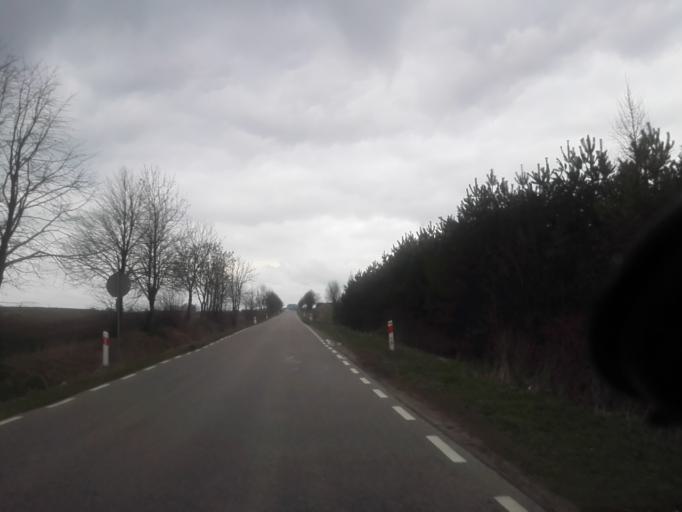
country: PL
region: Podlasie
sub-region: Suwalki
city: Suwalki
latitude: 54.2187
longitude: 22.9119
